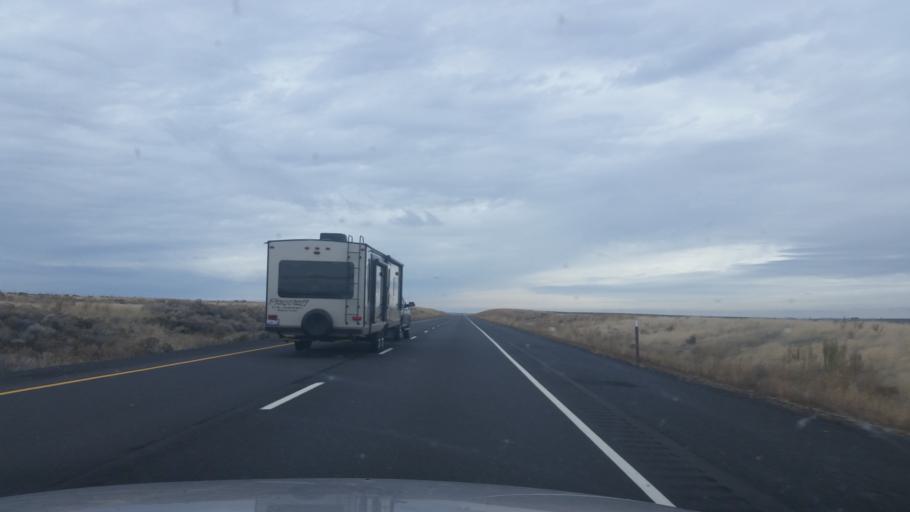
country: US
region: Washington
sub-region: Adams County
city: Ritzville
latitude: 47.0937
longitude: -118.6950
